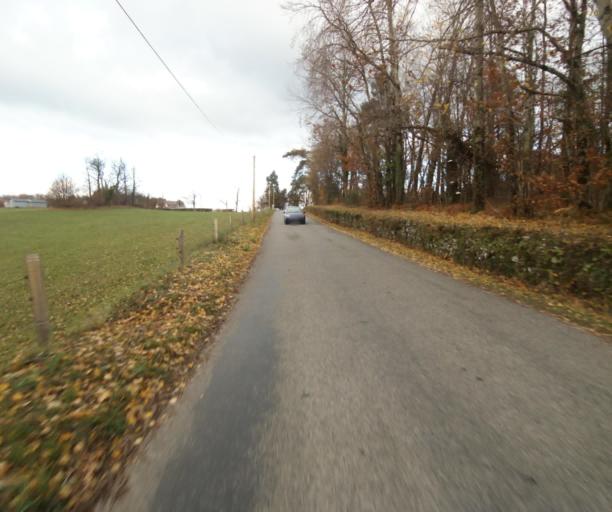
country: FR
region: Limousin
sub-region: Departement de la Correze
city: Sainte-Fortunade
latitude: 45.2112
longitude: 1.7793
